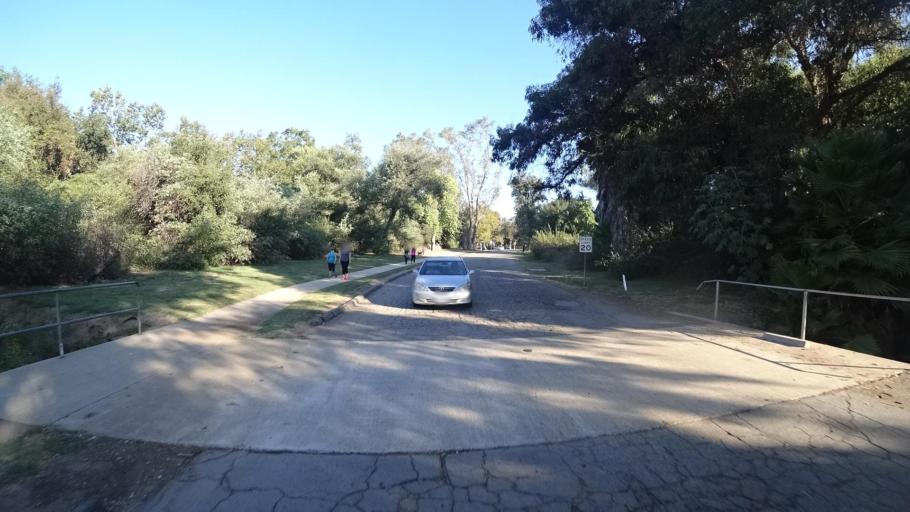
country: US
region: California
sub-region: San Diego County
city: Escondido
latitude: 33.0793
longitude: -117.0604
